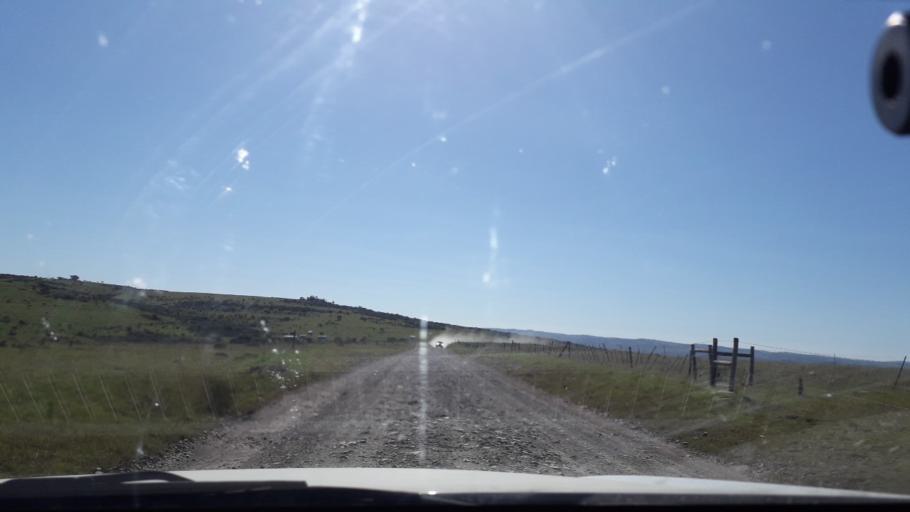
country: ZA
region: Eastern Cape
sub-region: Buffalo City Metropolitan Municipality
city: East London
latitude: -32.7963
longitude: 27.9512
